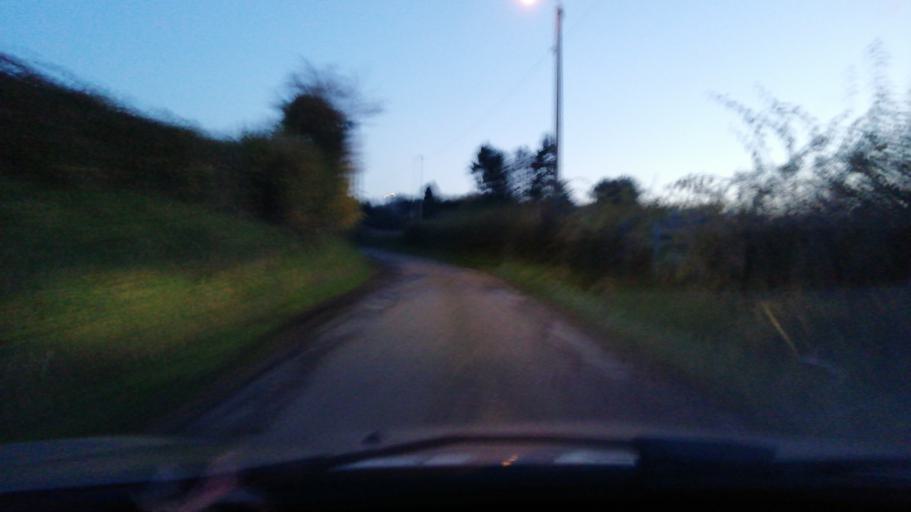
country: FR
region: Nord-Pas-de-Calais
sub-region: Departement du Nord
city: Marpent
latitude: 50.2541
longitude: 4.0916
